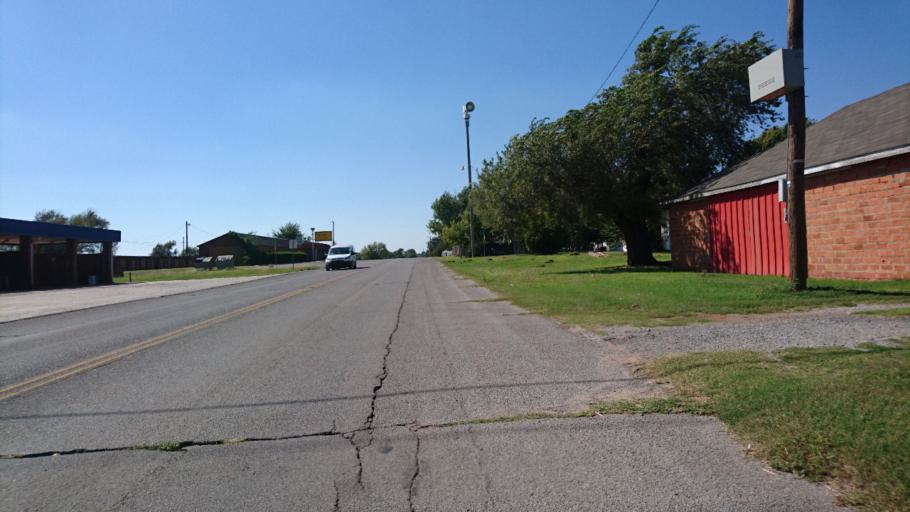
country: US
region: Oklahoma
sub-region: Custer County
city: Clinton
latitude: 35.5067
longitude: -98.9677
